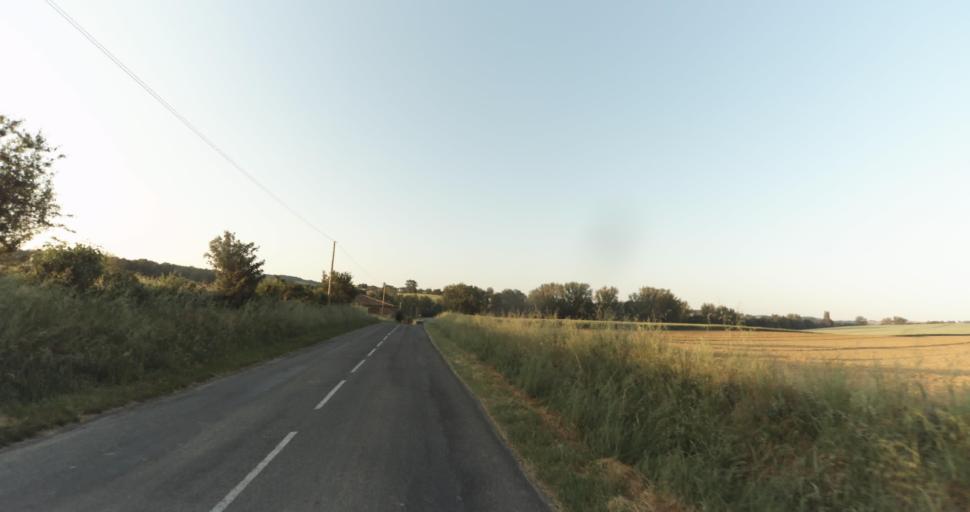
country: FR
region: Midi-Pyrenees
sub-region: Departement du Gers
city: Pujaudran
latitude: 43.6337
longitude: 1.1555
